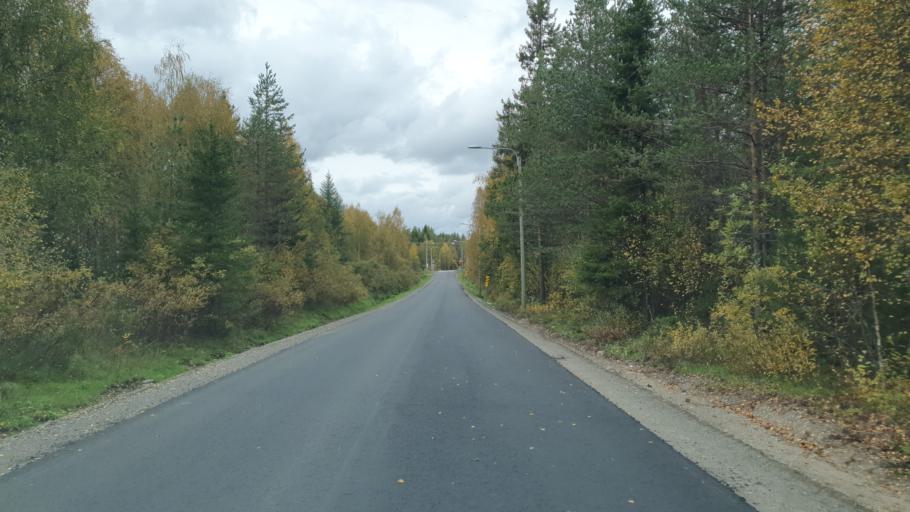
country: FI
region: Lapland
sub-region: Rovaniemi
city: Rovaniemi
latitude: 66.4195
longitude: 25.4123
